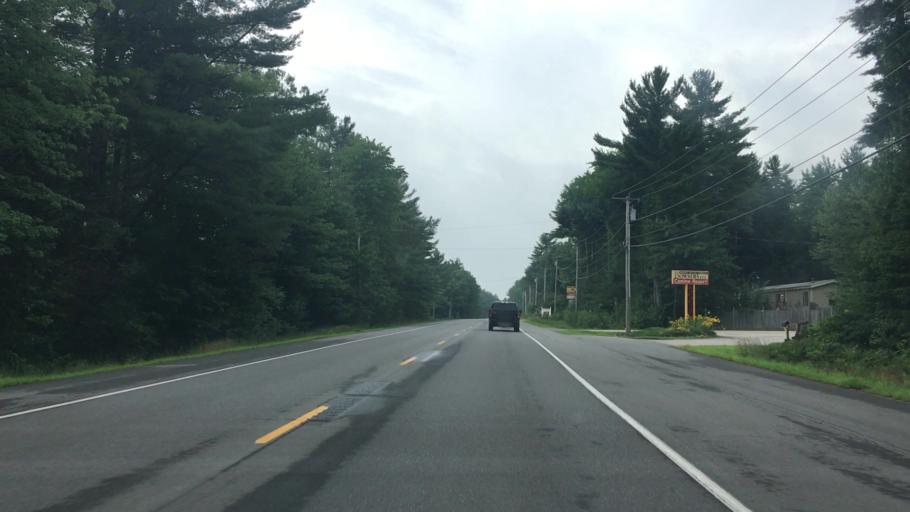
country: US
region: Maine
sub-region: York County
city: Lebanon
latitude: 43.3906
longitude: -70.8765
